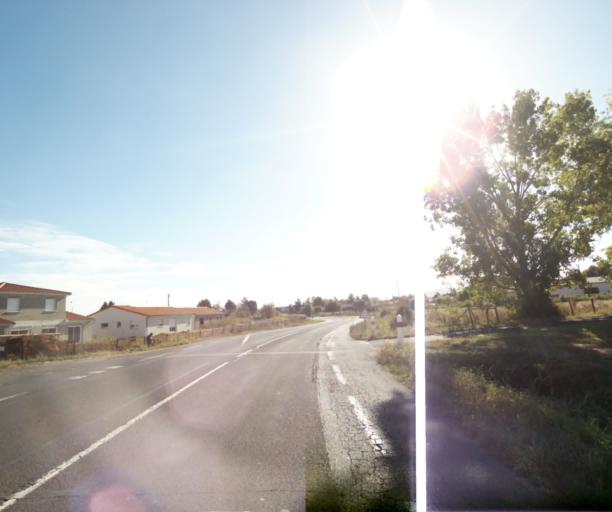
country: FR
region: Auvergne
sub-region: Departement du Puy-de-Dome
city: Malintrat
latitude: 45.8110
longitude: 3.1874
